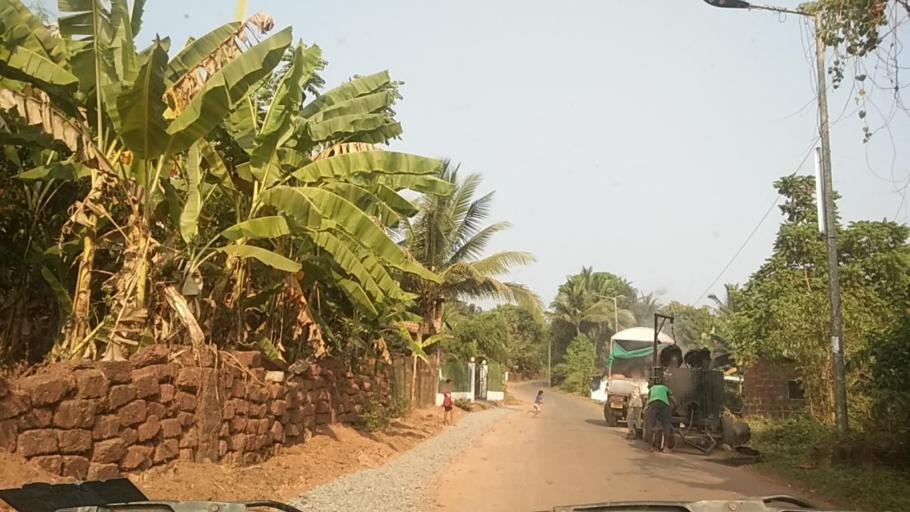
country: IN
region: Goa
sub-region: South Goa
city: Raia
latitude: 15.3165
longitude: 73.9482
